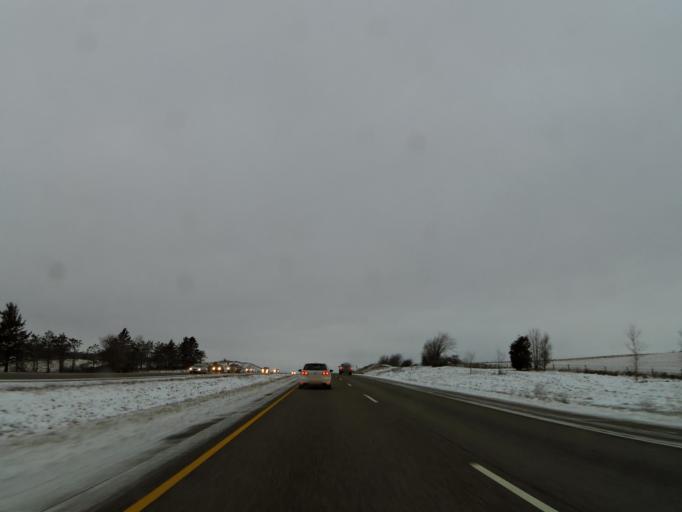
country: US
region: Wisconsin
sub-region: Saint Croix County
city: Hammond
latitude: 44.9417
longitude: -92.4873
